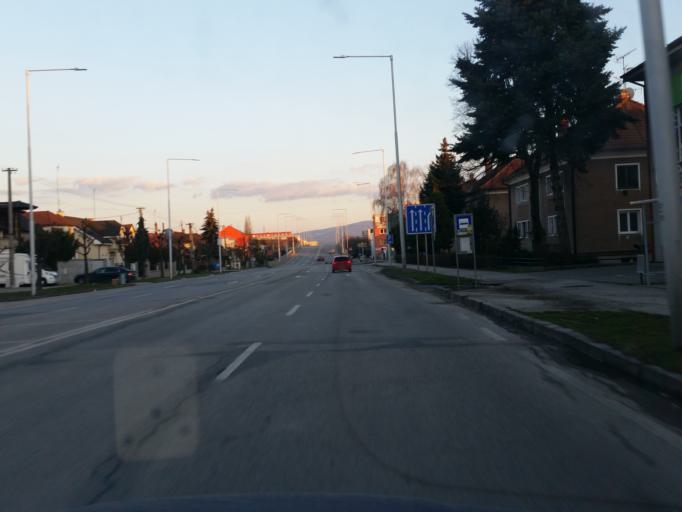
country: SK
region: Nitriansky
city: Banovce nad Bebravou
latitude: 48.5621
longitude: 18.1622
